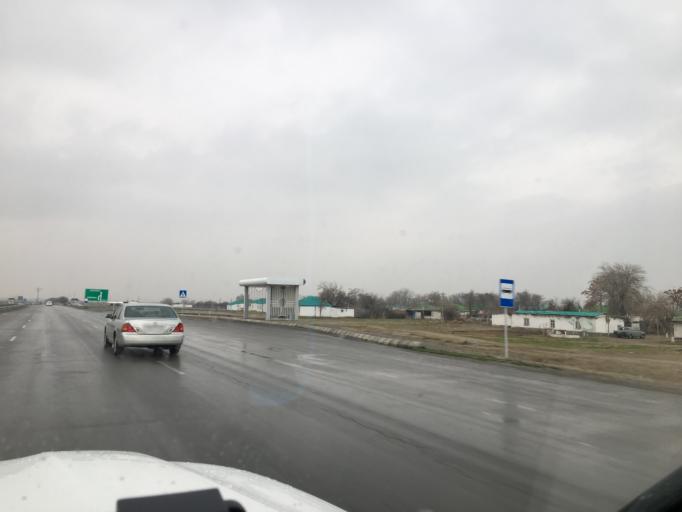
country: TM
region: Ahal
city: Annau
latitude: 37.8278
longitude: 58.7501
